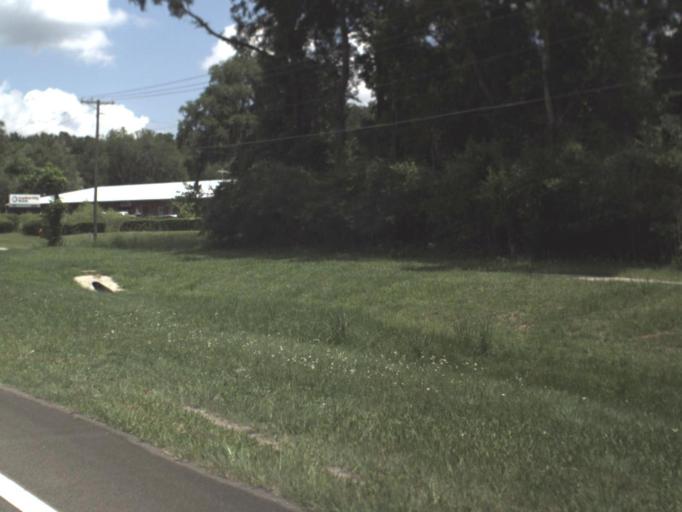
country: US
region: Florida
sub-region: Alachua County
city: High Springs
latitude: 29.8238
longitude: -82.5888
